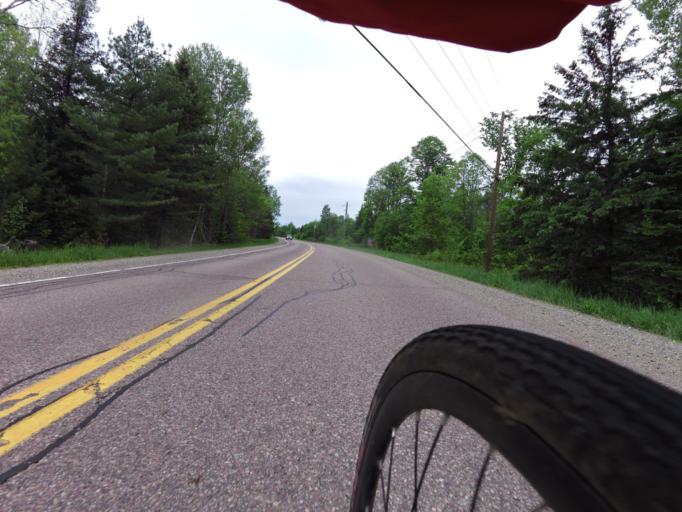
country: CA
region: Ontario
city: Renfrew
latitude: 45.2899
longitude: -76.6890
